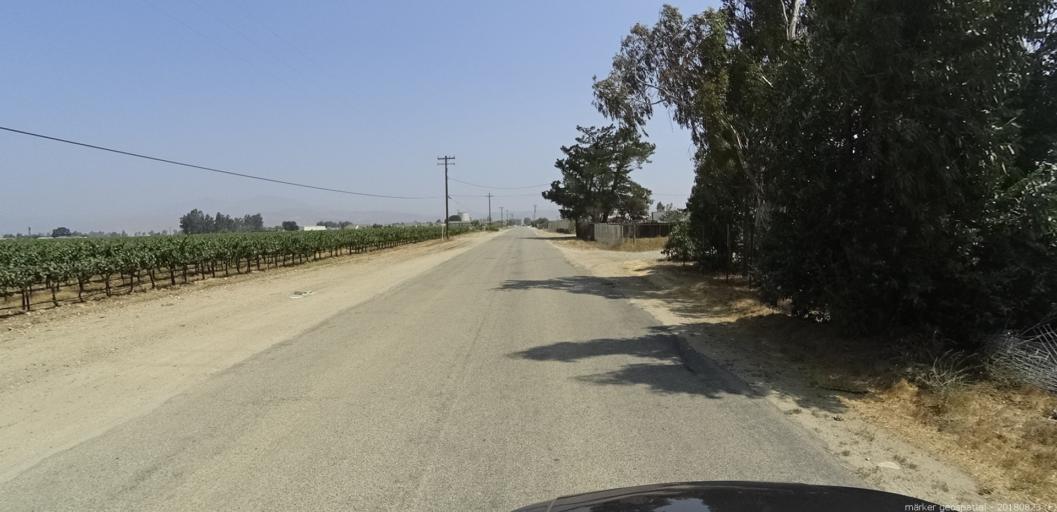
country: US
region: California
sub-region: Monterey County
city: Greenfield
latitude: 36.3198
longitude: -121.2610
